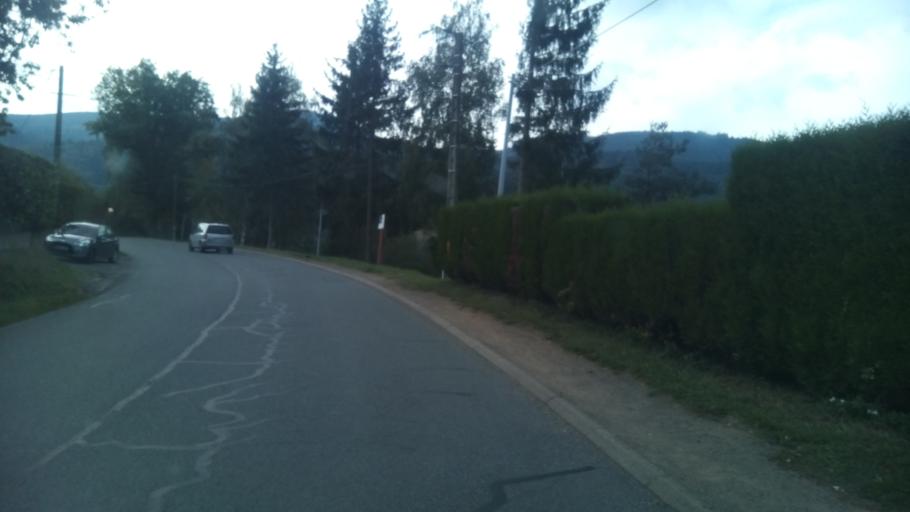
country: FR
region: Bourgogne
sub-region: Departement de Saone-et-Loire
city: Matour
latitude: 46.2224
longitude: 4.5160
